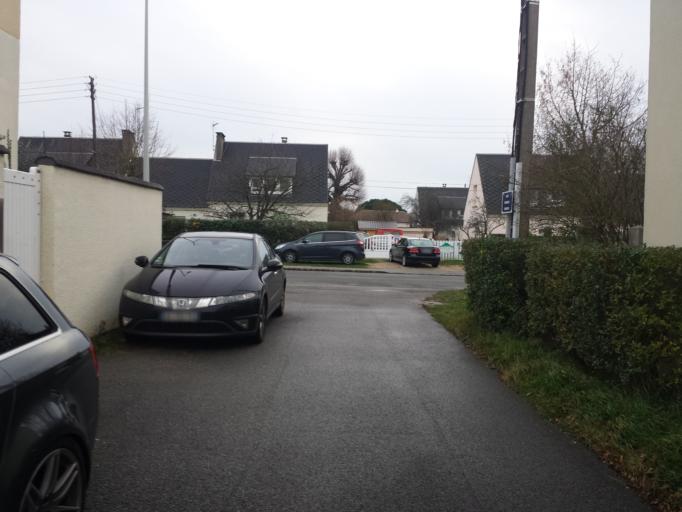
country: FR
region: Haute-Normandie
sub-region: Departement de l'Eure
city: Evreux
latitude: 49.0186
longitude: 1.1656
